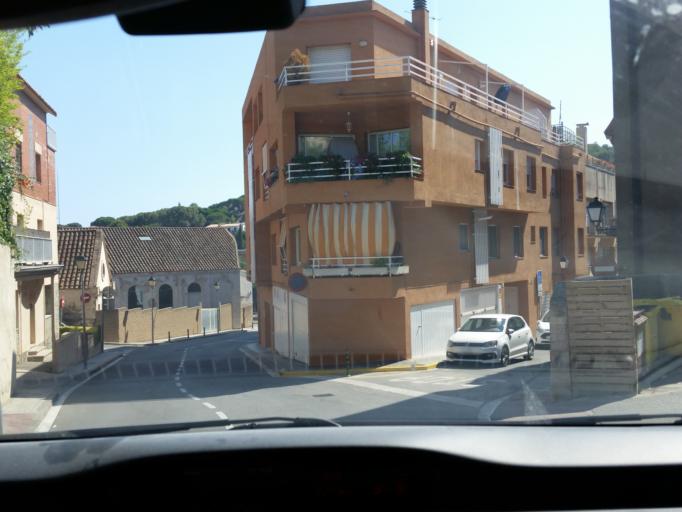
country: ES
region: Catalonia
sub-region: Provincia de Barcelona
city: Cabrils
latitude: 41.5273
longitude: 2.3652
